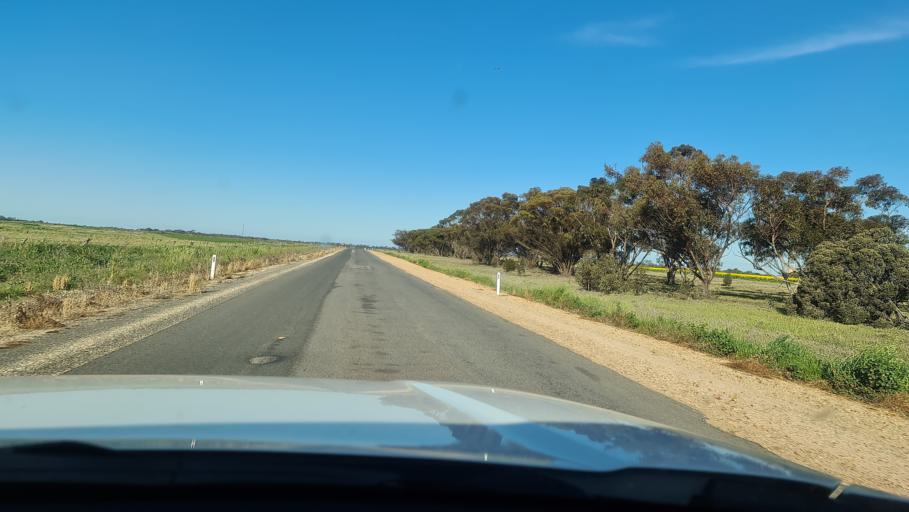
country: AU
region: Victoria
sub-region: Horsham
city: Horsham
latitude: -36.4492
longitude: 142.5653
